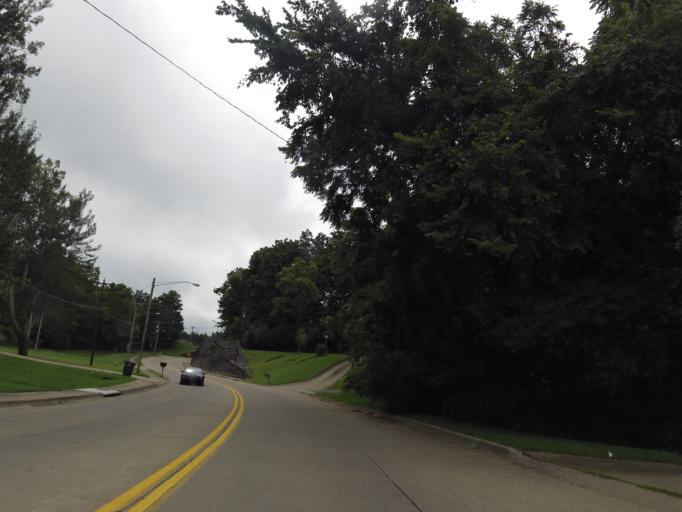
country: US
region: Missouri
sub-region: Cape Girardeau County
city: Cape Girardeau
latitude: 37.3501
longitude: -89.5603
